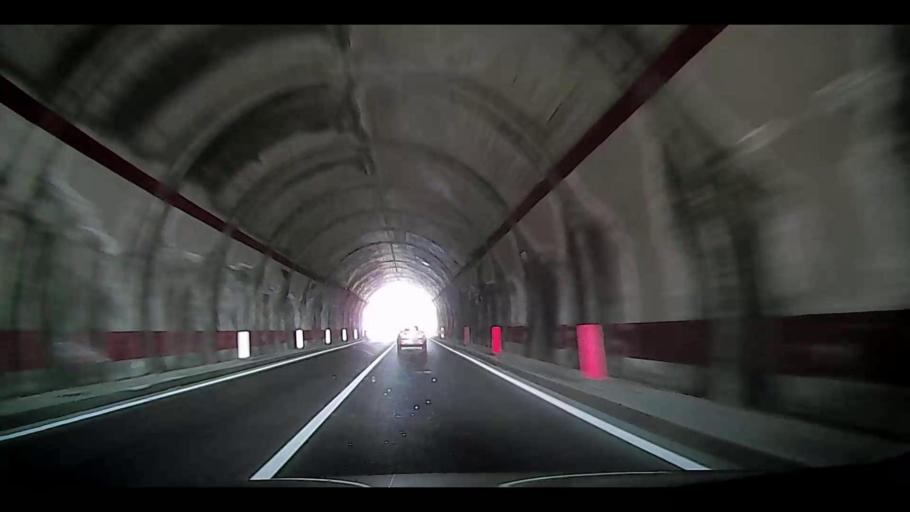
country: IT
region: Calabria
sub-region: Provincia di Crotone
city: Caccuri
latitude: 39.2193
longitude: 16.7950
